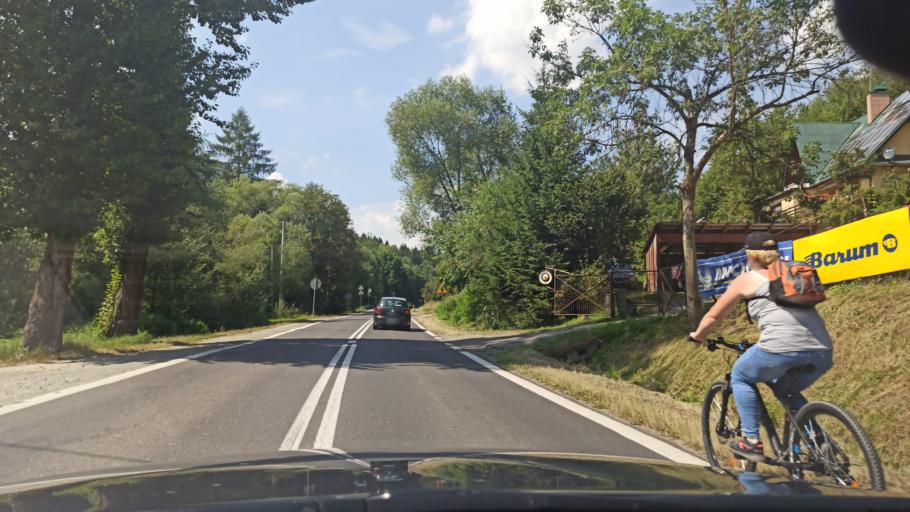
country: PL
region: Lesser Poland Voivodeship
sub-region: Powiat nowotarski
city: Krosnica
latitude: 49.4381
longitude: 20.3610
